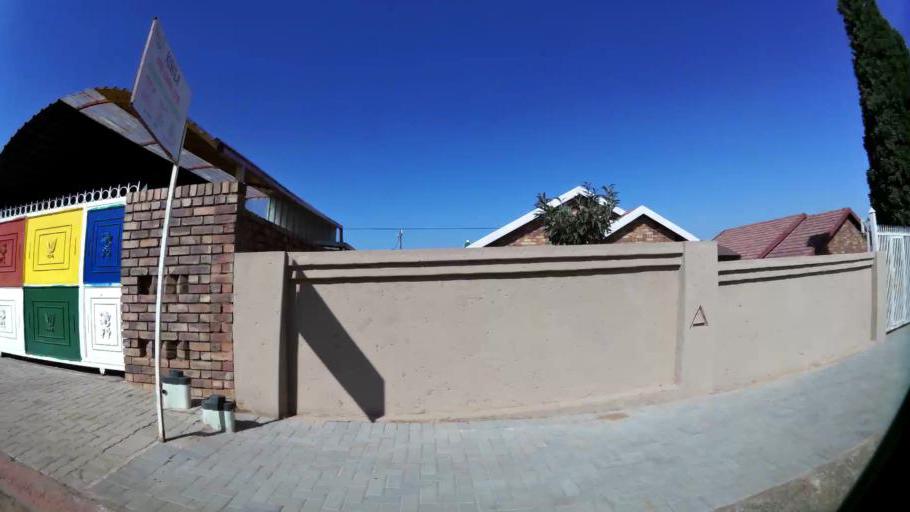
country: ZA
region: Gauteng
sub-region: City of Tshwane Metropolitan Municipality
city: Mabopane
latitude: -25.5618
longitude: 28.0808
